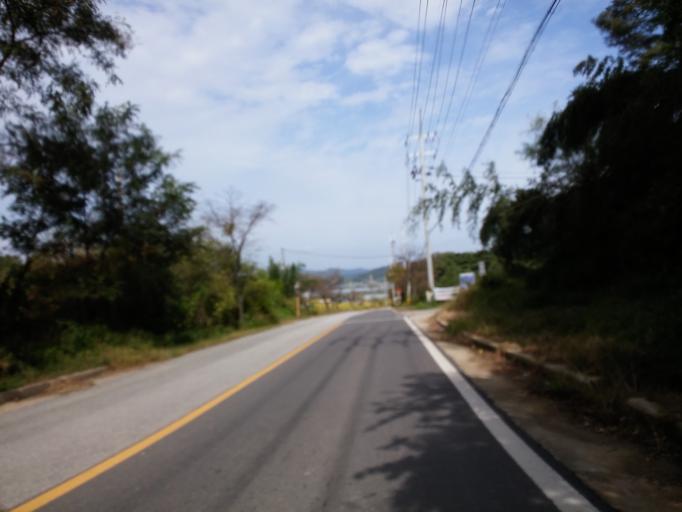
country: KR
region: Chungcheongnam-do
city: Nonsan
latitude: 36.1731
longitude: 127.1216
